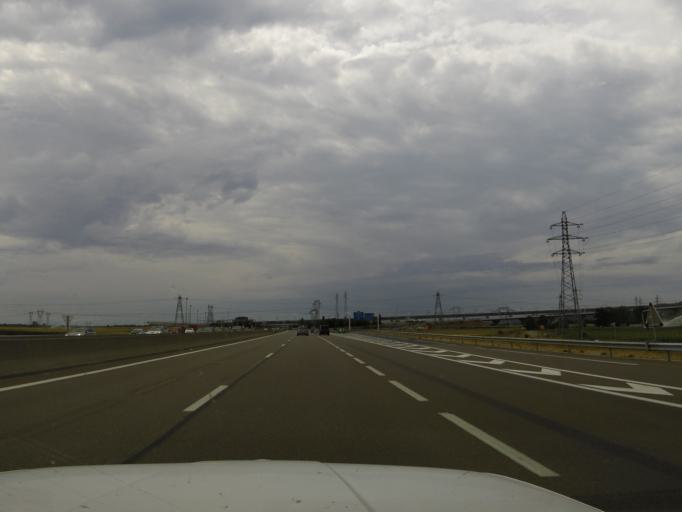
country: FR
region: Rhone-Alpes
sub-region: Departement de l'Ain
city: La Boisse
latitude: 45.8359
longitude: 5.0355
